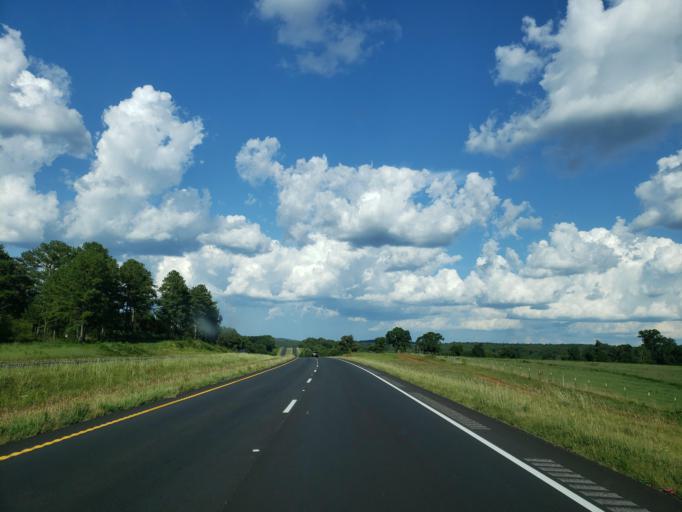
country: US
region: Georgia
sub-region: Floyd County
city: Lindale
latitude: 34.2063
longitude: -85.0836
